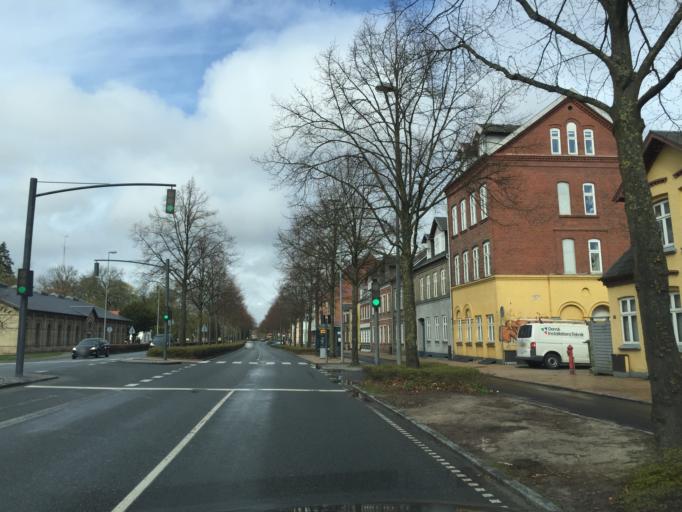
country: DK
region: South Denmark
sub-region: Odense Kommune
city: Odense
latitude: 55.3869
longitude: 10.3748
